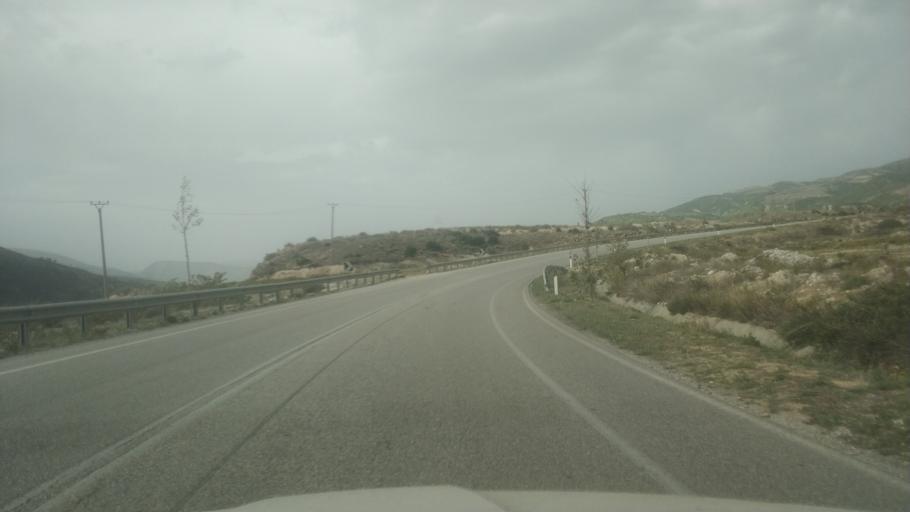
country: AL
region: Gjirokaster
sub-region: Rrethi i Tepelenes
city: Memaliaj
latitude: 40.3649
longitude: 19.9093
